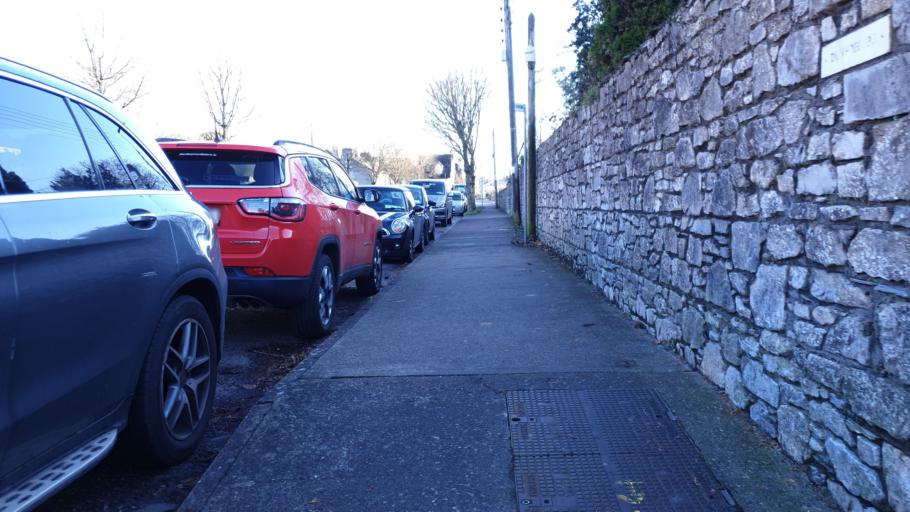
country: IE
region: Munster
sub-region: County Cork
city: Cork
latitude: 51.8912
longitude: -8.4480
